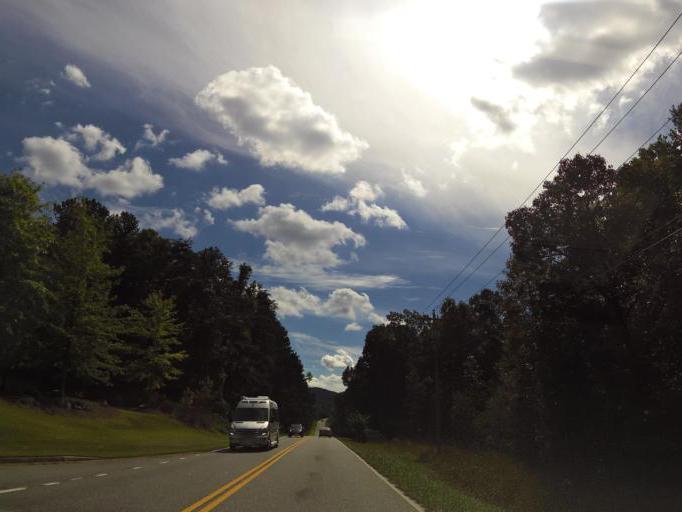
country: US
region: Georgia
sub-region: Pickens County
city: Nelson
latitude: 34.4606
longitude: -84.2604
